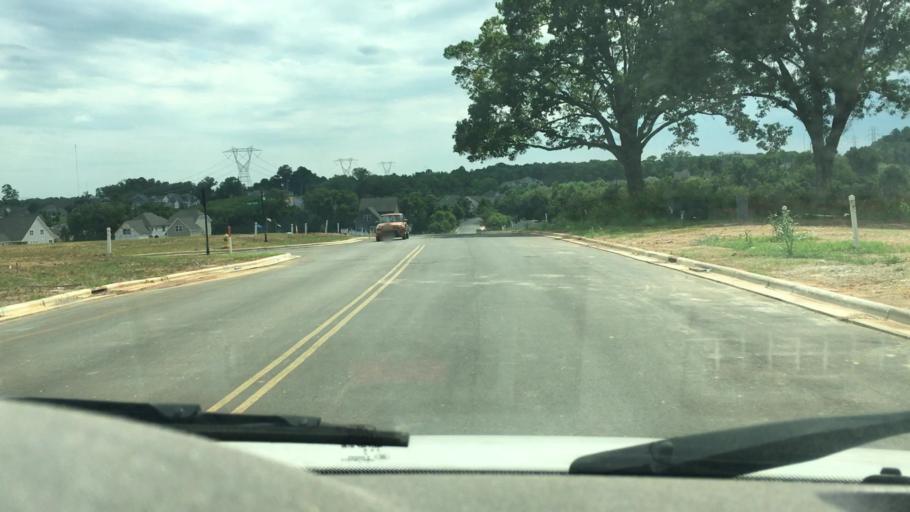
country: US
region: North Carolina
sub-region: Gaston County
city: Davidson
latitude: 35.4775
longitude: -80.8209
